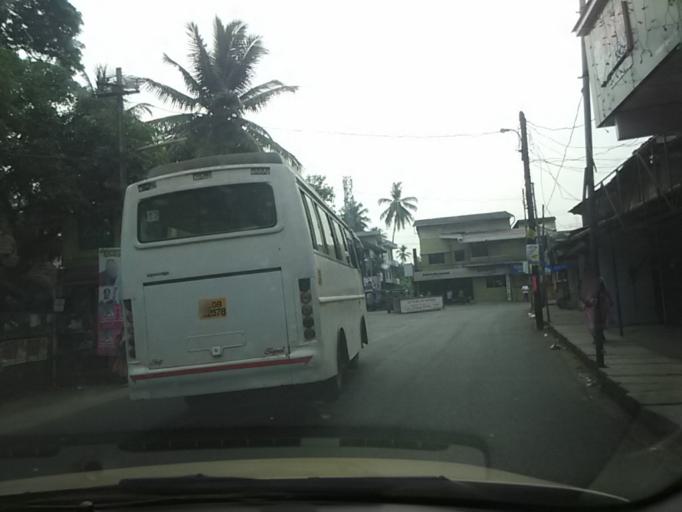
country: IN
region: Kerala
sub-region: Kozhikode
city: Kozhikode
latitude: 11.2727
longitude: 75.7769
